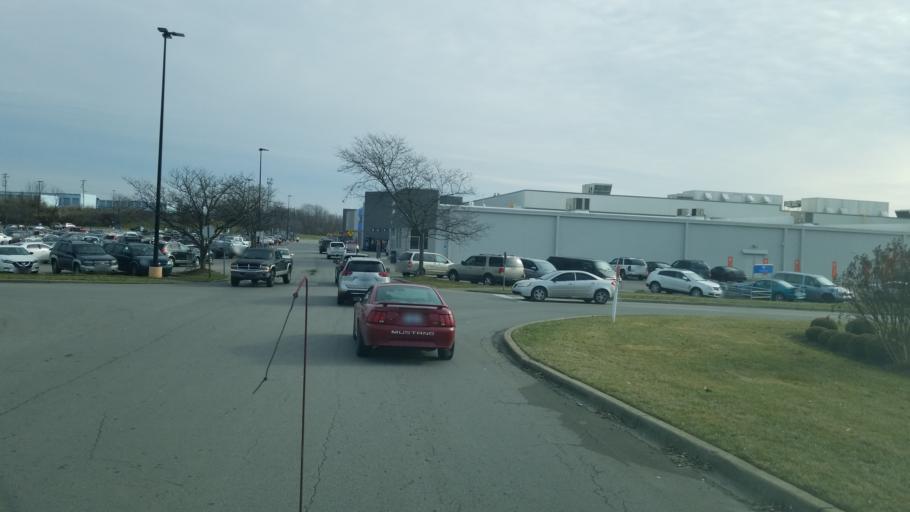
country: US
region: Kentucky
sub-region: Boyle County
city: Danville
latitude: 37.6147
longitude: -84.7737
